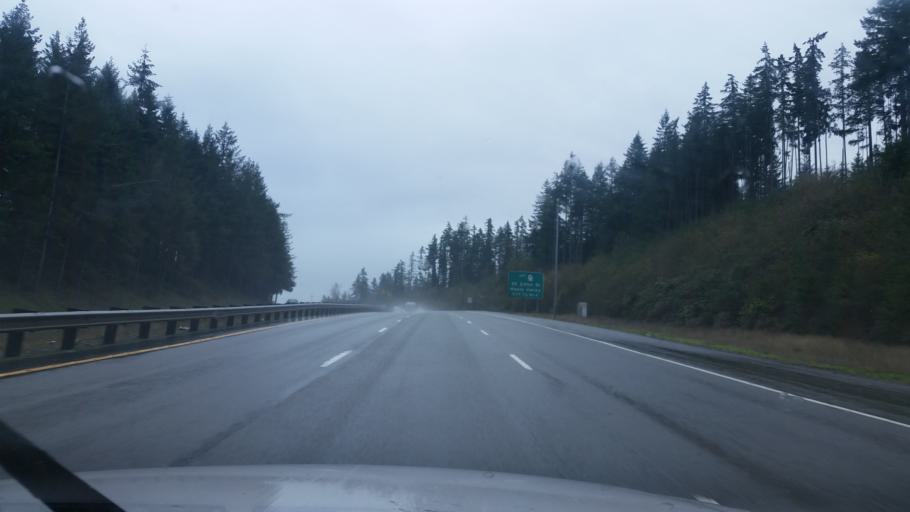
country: US
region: Washington
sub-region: King County
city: Maple Valley
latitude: 47.4039
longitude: -122.0436
